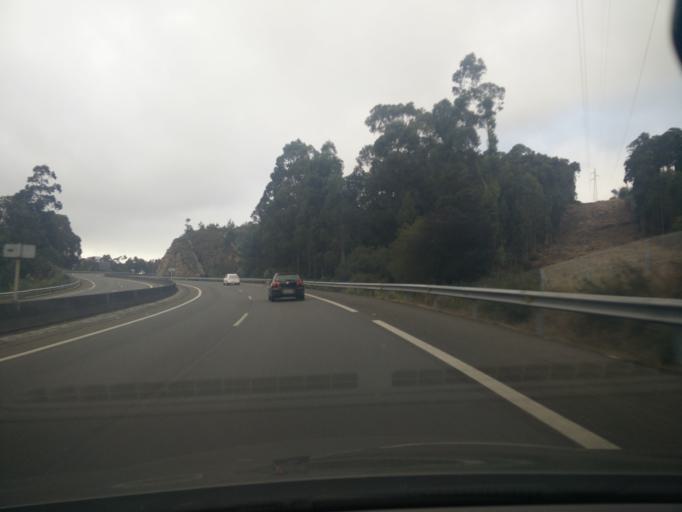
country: ES
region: Galicia
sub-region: Provincia da Coruna
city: Arteixo
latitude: 43.3168
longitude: -8.4704
